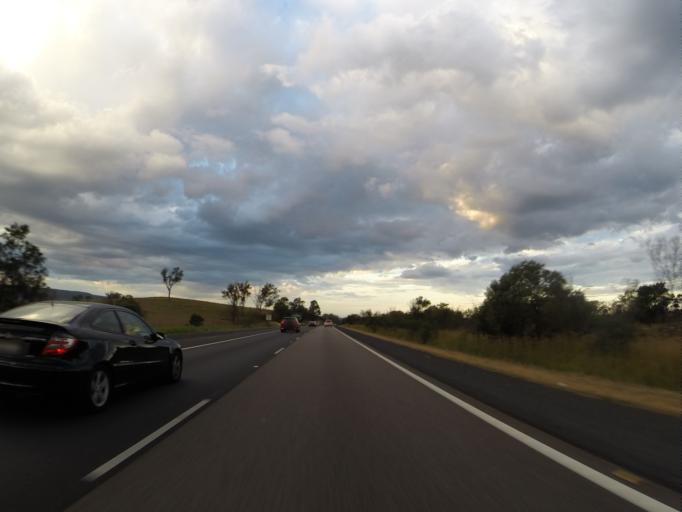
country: AU
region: New South Wales
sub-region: Wollondilly
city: Douglas Park
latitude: -34.2213
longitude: 150.6757
